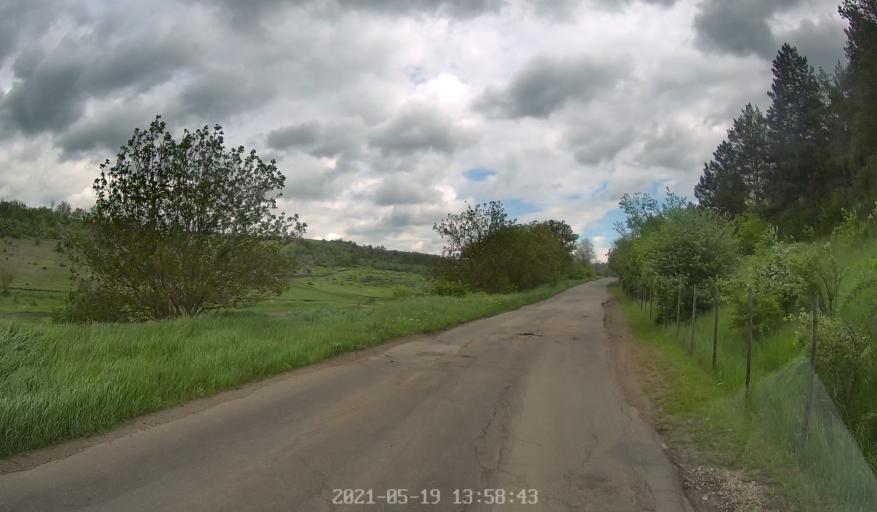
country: MD
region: Chisinau
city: Chisinau
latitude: 47.0431
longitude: 28.9190
